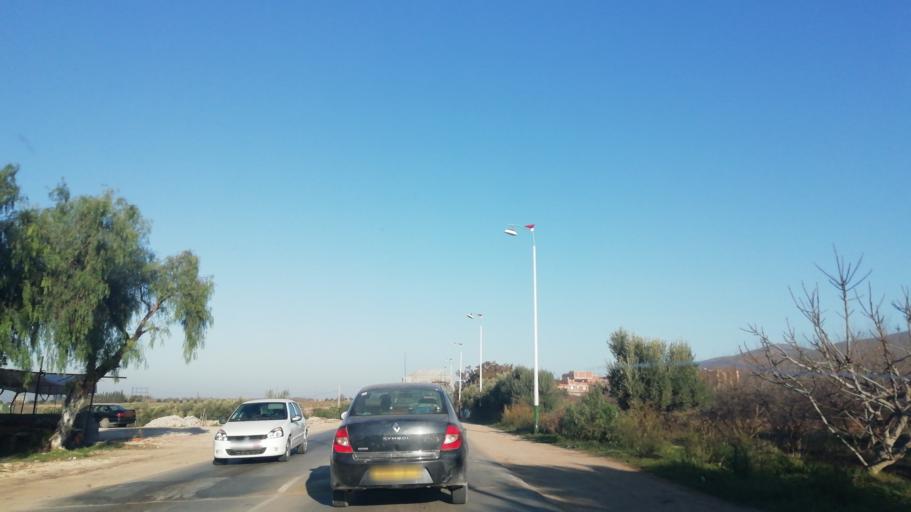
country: MA
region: Oriental
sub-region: Berkane-Taourirt
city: Ahfir
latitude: 34.9772
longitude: -2.1042
